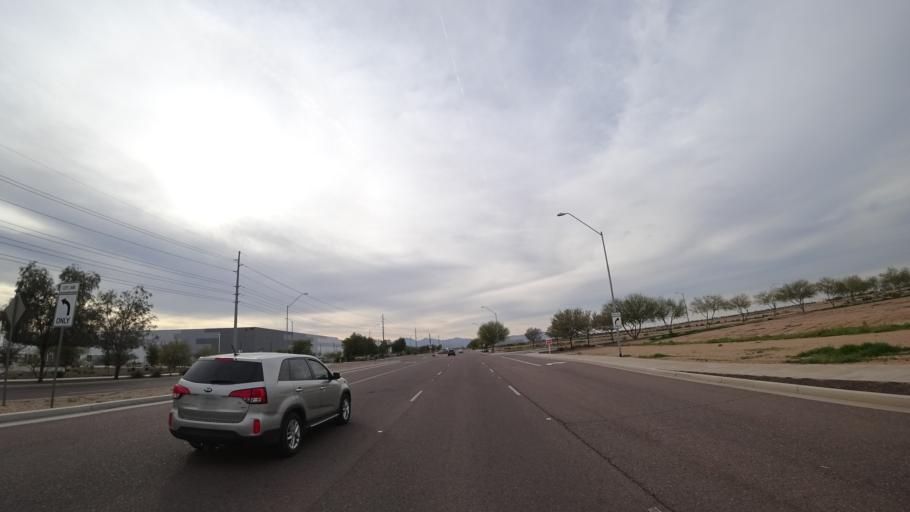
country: US
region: Arizona
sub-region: Maricopa County
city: El Mirage
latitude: 33.5947
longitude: -112.3463
